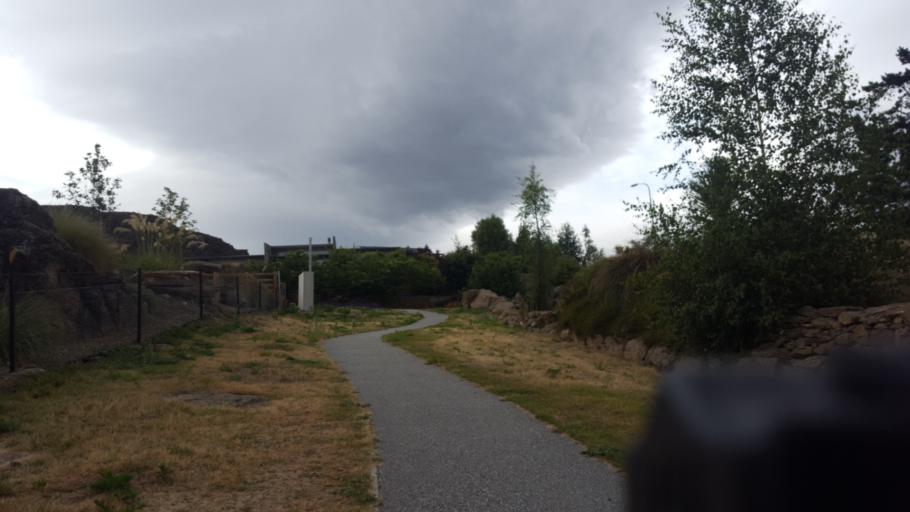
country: NZ
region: Otago
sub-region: Queenstown-Lakes District
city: Wanaka
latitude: -45.2512
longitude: 169.4033
